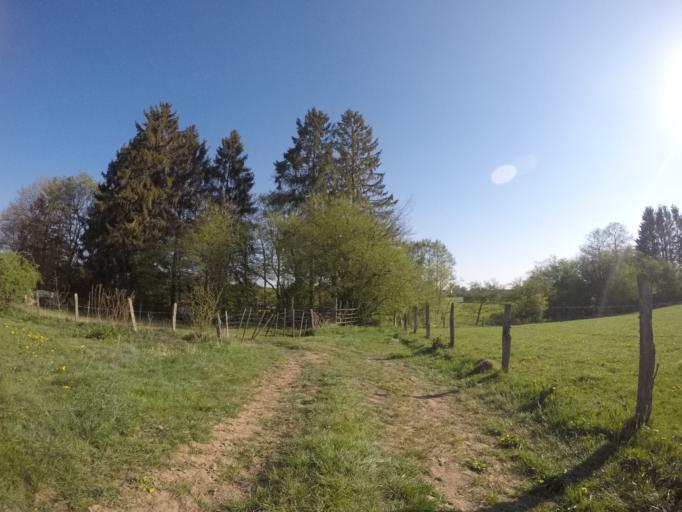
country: BE
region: Wallonia
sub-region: Province du Luxembourg
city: Tintigny
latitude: 49.7124
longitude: 5.5416
